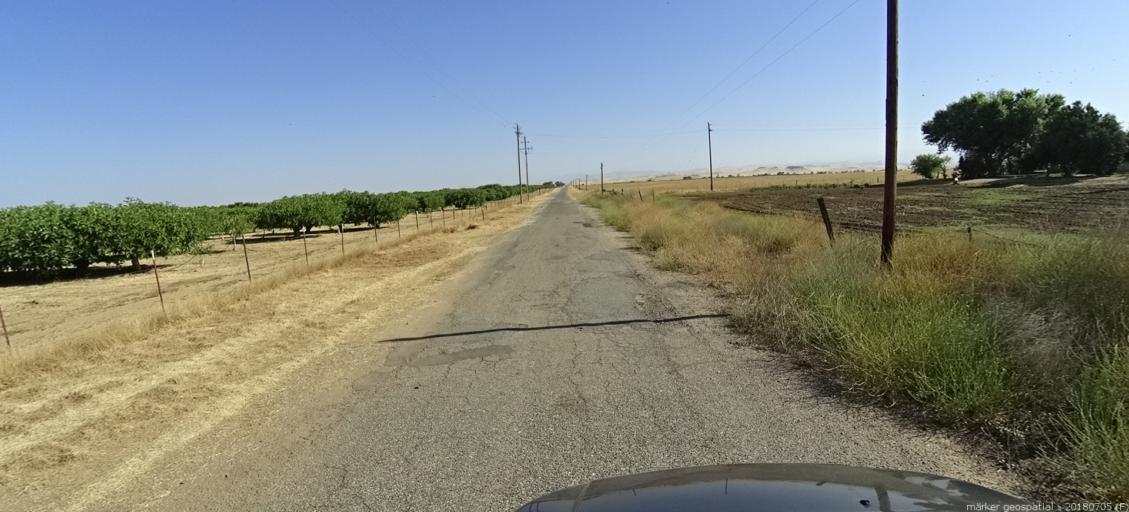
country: US
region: California
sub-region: Madera County
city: Madera Acres
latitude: 37.1514
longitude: -120.0748
